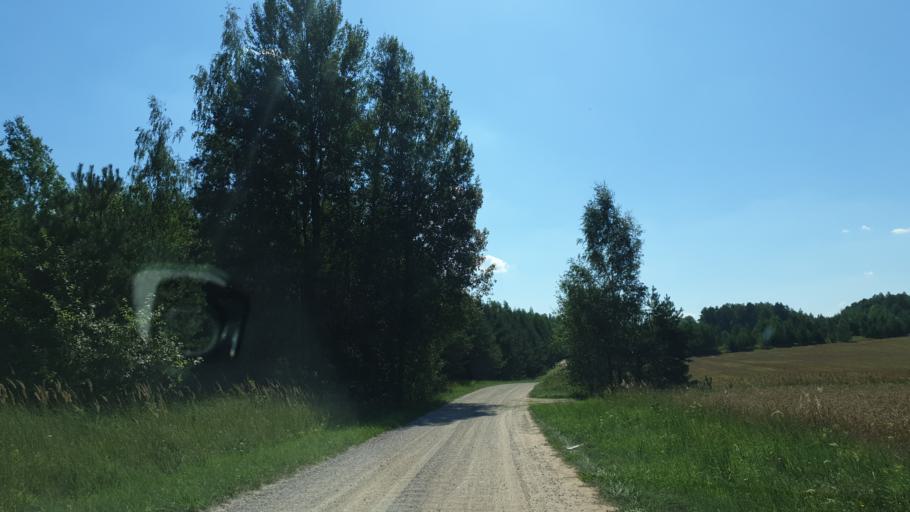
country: LT
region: Vilnius County
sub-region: Vilniaus Rajonas
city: Vievis
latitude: 54.9030
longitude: 24.8788
